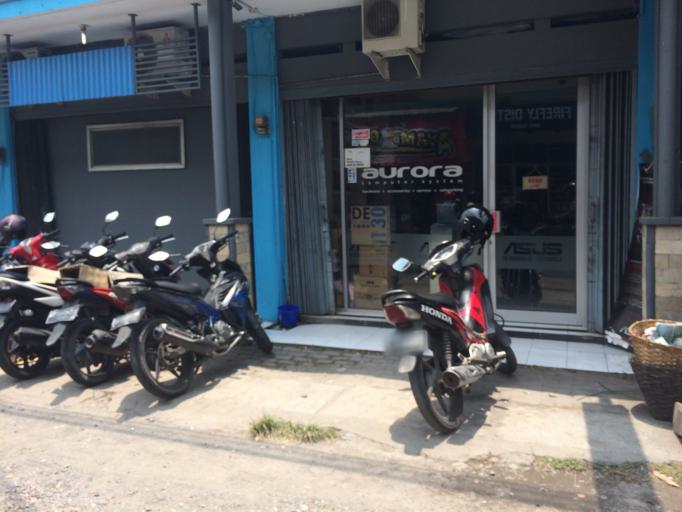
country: ID
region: Central Java
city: Colomadu
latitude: -7.5543
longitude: 110.7688
